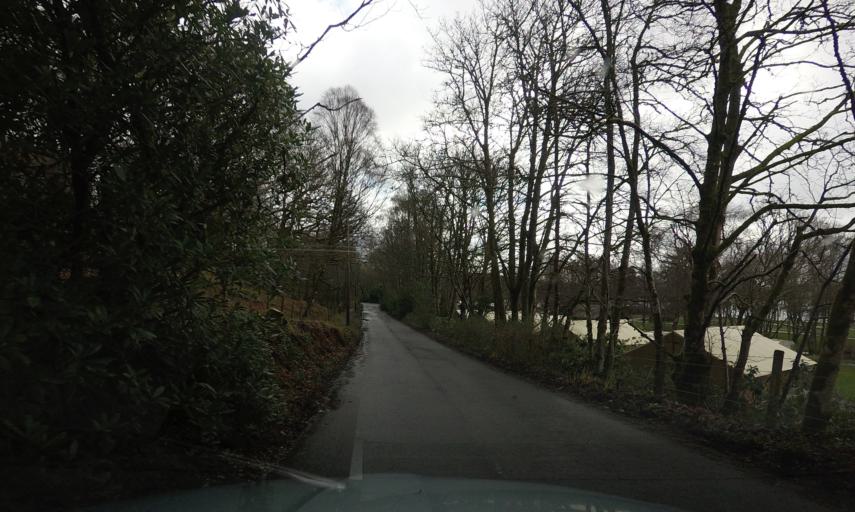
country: GB
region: Scotland
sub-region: West Dunbartonshire
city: Balloch
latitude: 56.1013
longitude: -4.5631
